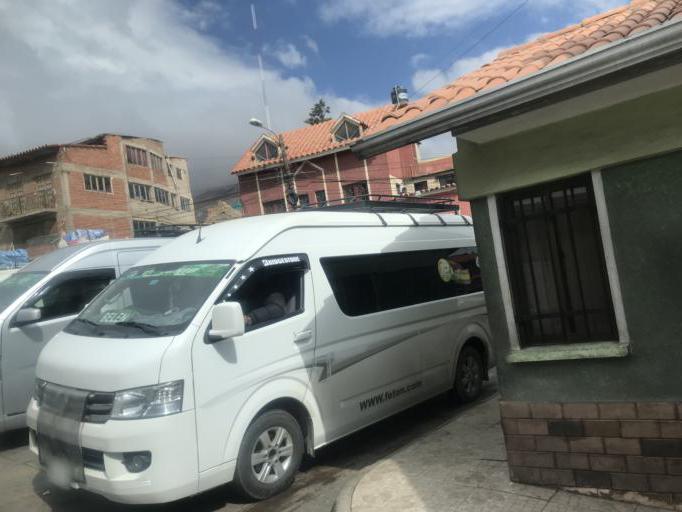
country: BO
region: Potosi
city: Potosi
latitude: -19.5947
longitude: -65.7503
